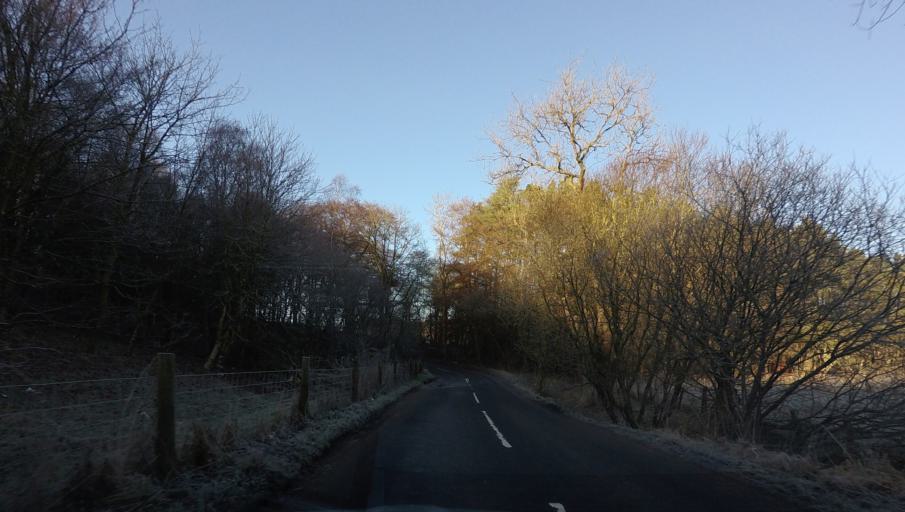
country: GB
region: Scotland
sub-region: North Lanarkshire
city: Shotts
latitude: 55.8048
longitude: -3.8427
